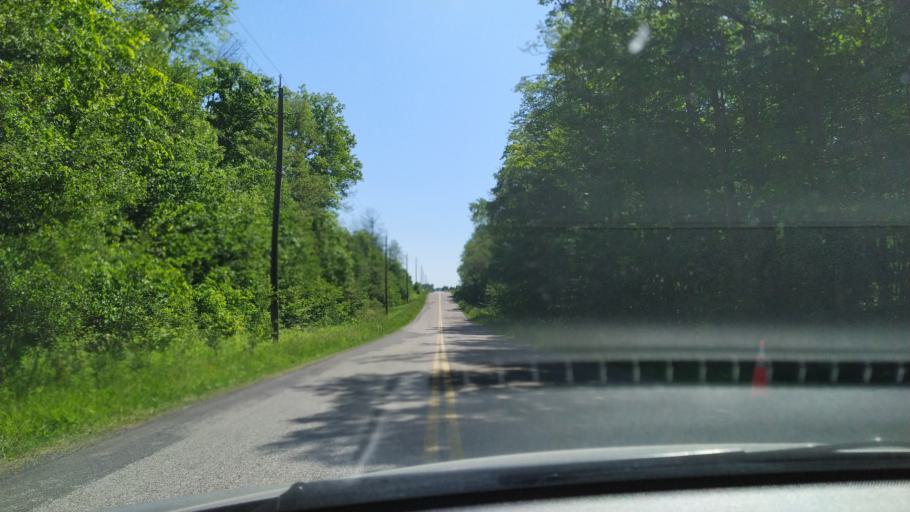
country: CA
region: Ontario
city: Waterloo
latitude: 43.4585
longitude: -80.7206
